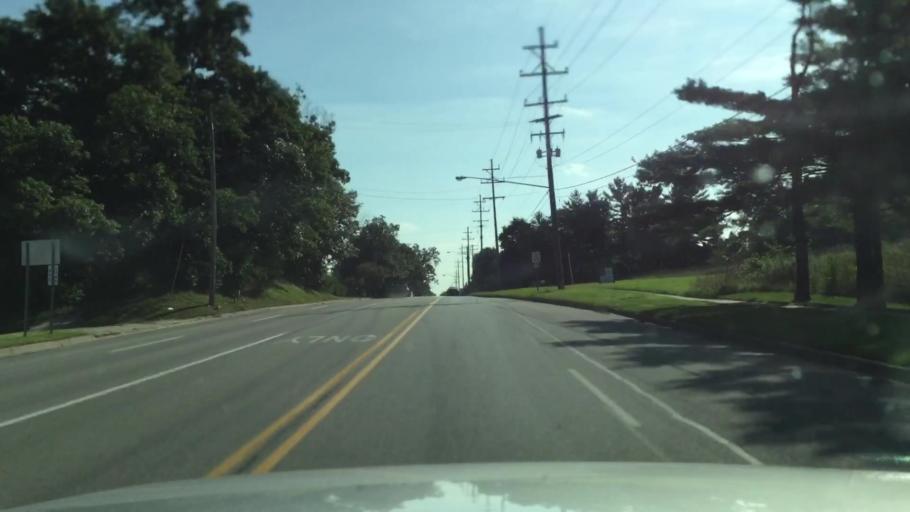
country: US
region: Michigan
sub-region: Kalamazoo County
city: Portage
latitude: 42.2450
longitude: -85.5864
